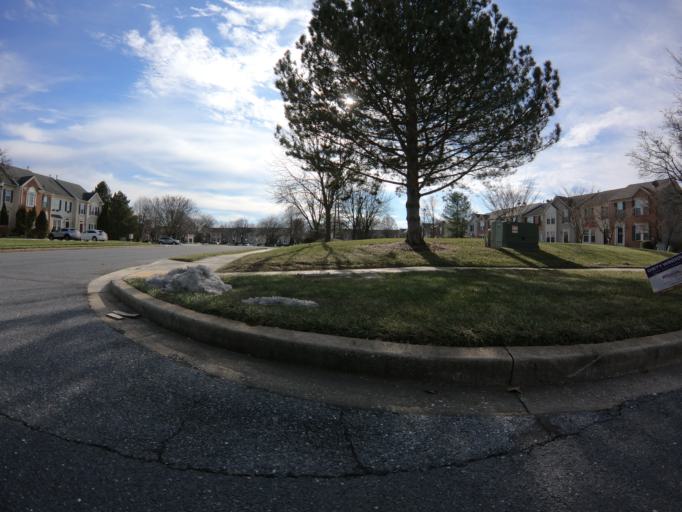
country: US
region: Maryland
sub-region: Frederick County
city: Ballenger Creek
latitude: 39.3822
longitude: -77.4405
